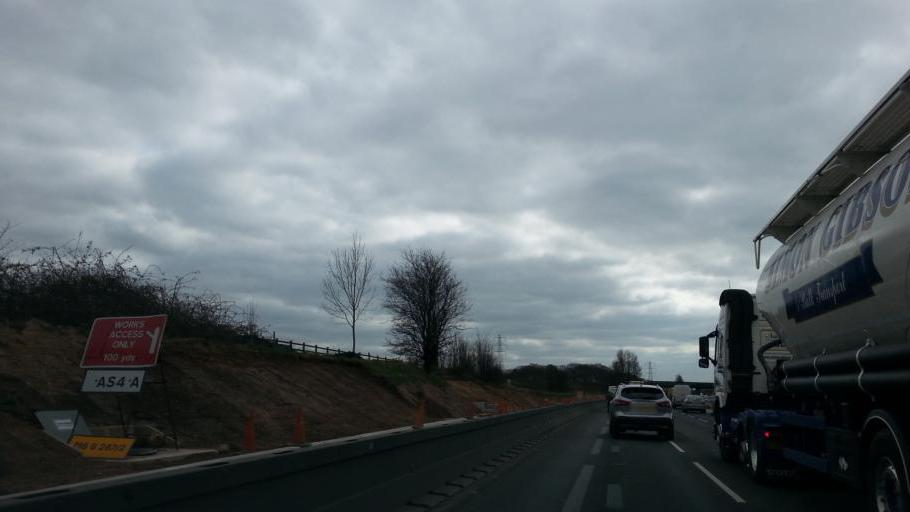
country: GB
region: England
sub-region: Cheshire East
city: Knutsford
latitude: 53.2899
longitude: -2.3956
